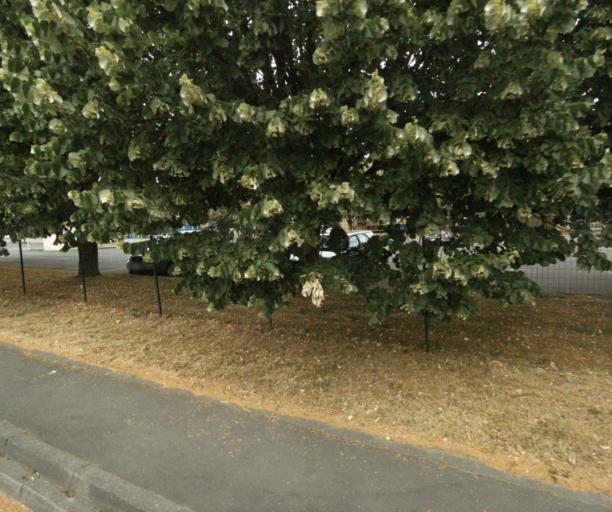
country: FR
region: Nord-Pas-de-Calais
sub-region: Departement du Nord
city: Neuville-en-Ferrain
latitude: 50.7571
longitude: 3.1628
